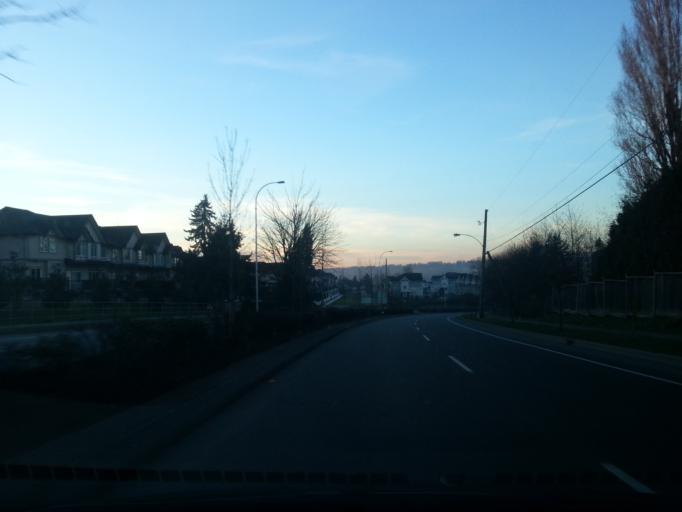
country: CA
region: British Columbia
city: Langley
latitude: 49.1319
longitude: -122.7216
